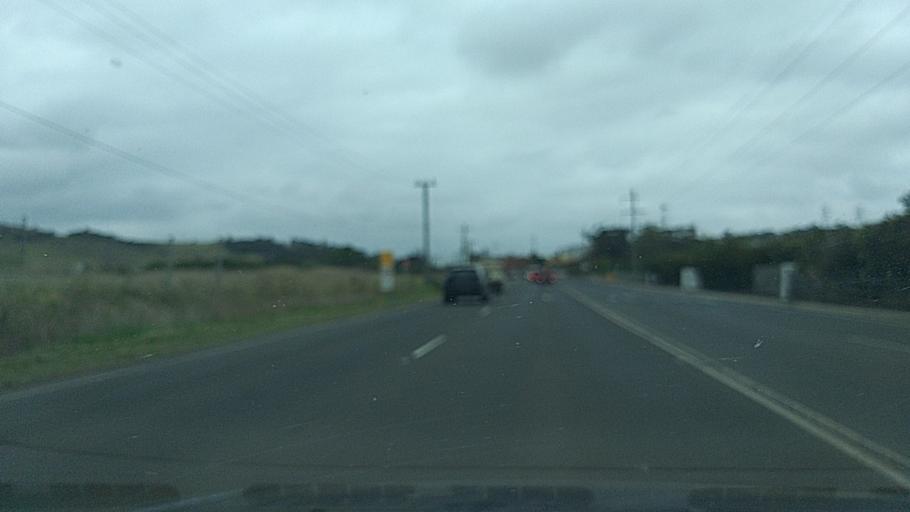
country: AU
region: New South Wales
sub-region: Wollongong
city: Berkeley
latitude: -34.4691
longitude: 150.8234
